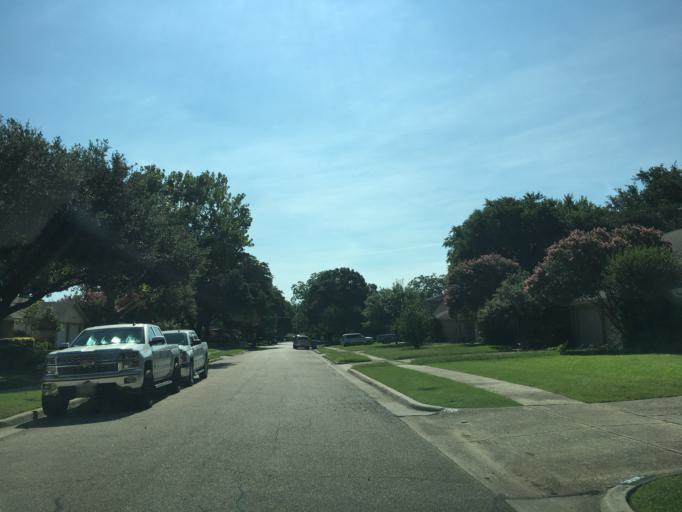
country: US
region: Texas
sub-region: Dallas County
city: Farmers Branch
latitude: 32.9193
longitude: -96.8805
